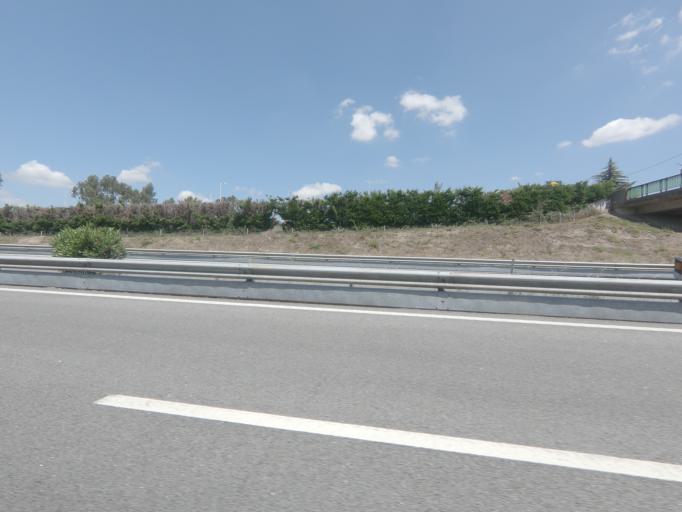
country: PT
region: Porto
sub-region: Paredes
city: Casteloes de Cepeda
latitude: 41.1986
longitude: -8.3348
